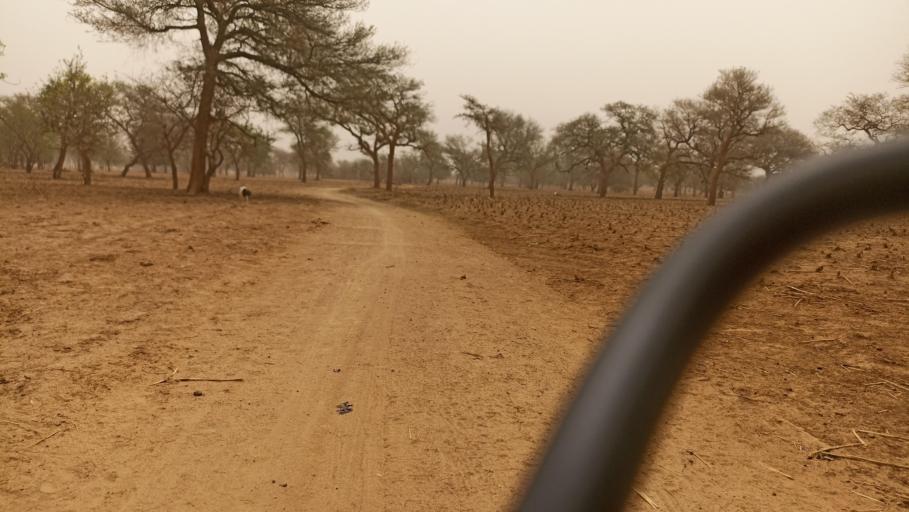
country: BF
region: Nord
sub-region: Province du Zondoma
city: Gourcy
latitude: 13.2496
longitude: -2.6000
